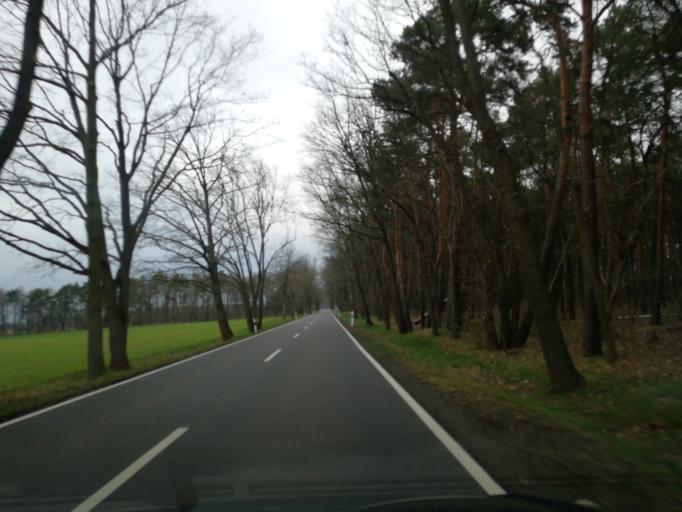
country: DE
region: Brandenburg
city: Vetschau
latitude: 51.7468
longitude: 14.0522
